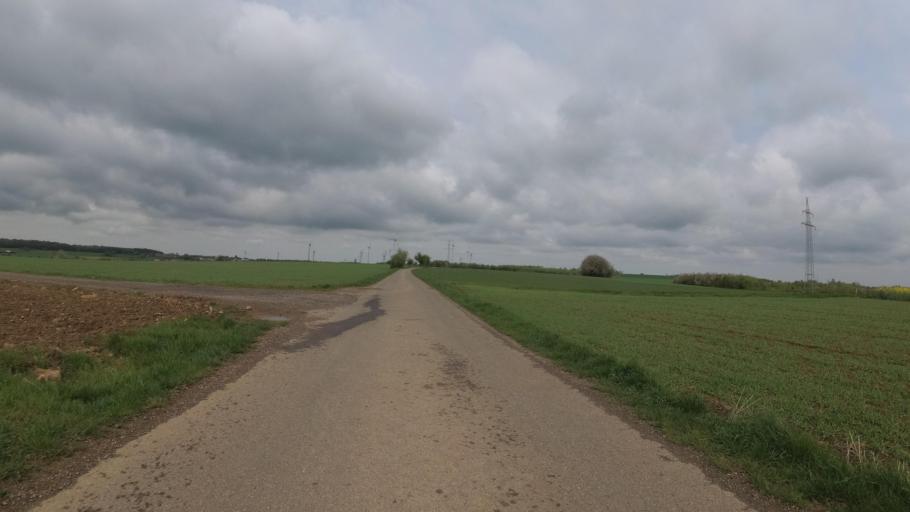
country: DE
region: Saarland
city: Orscholz
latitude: 49.4431
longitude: 6.5114
